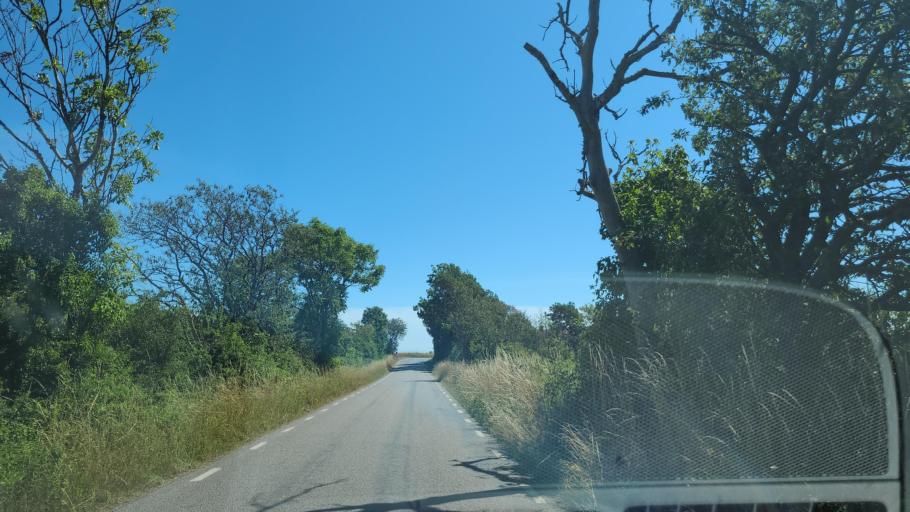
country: SE
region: Kalmar
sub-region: Borgholms Kommun
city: Borgholm
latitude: 56.7436
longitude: 16.7027
